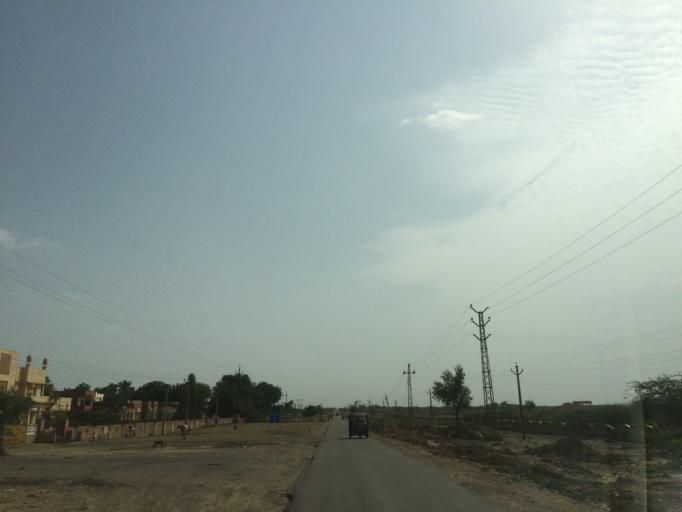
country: IN
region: Rajasthan
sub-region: Jaisalmer
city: Jaisalmer
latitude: 26.9027
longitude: 70.9319
